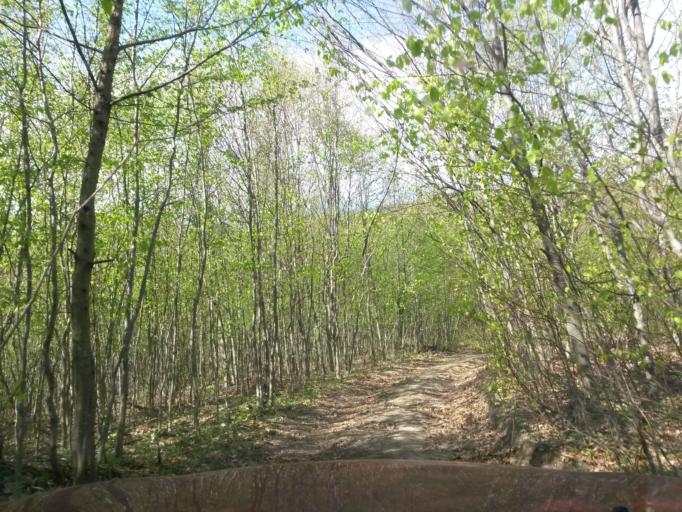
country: SK
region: Presovsky
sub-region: Okres Presov
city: Presov
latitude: 48.9487
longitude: 21.1360
